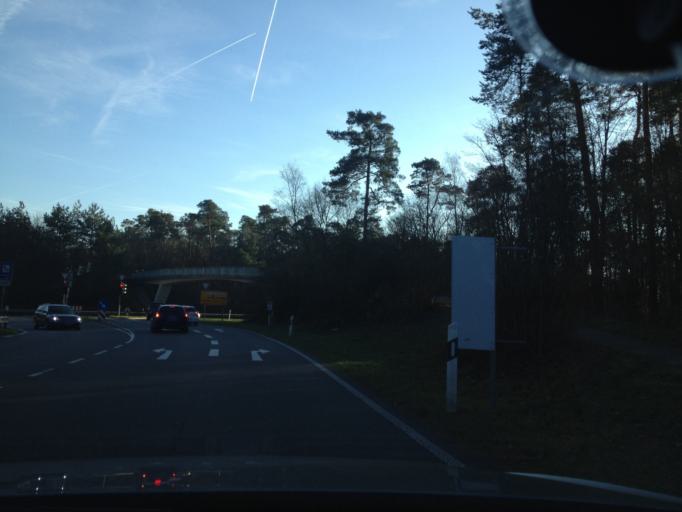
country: DE
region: Baden-Wuerttemberg
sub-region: Karlsruhe Region
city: Walldorf
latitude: 49.3189
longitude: 8.6314
